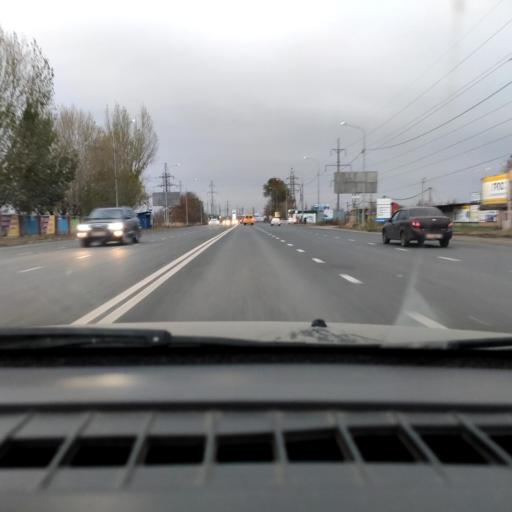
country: RU
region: Samara
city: Tol'yatti
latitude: 53.5755
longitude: 49.2931
